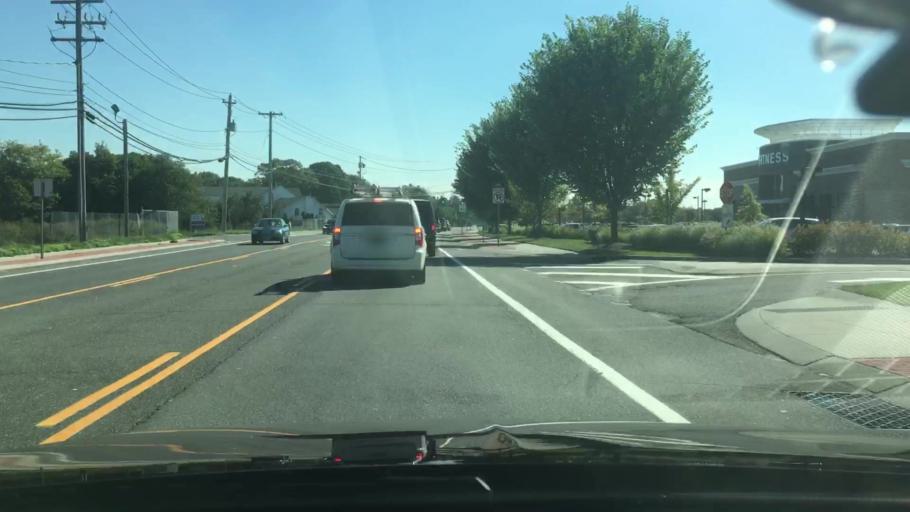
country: US
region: New York
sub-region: Suffolk County
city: Port Jefferson Station
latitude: 40.9215
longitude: -73.0431
